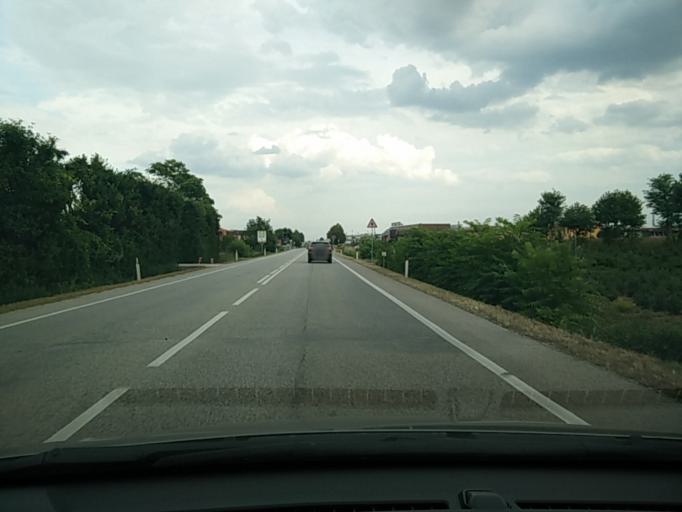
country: IT
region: Veneto
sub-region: Provincia di Treviso
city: Salvatronda
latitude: 45.6849
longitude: 11.9894
